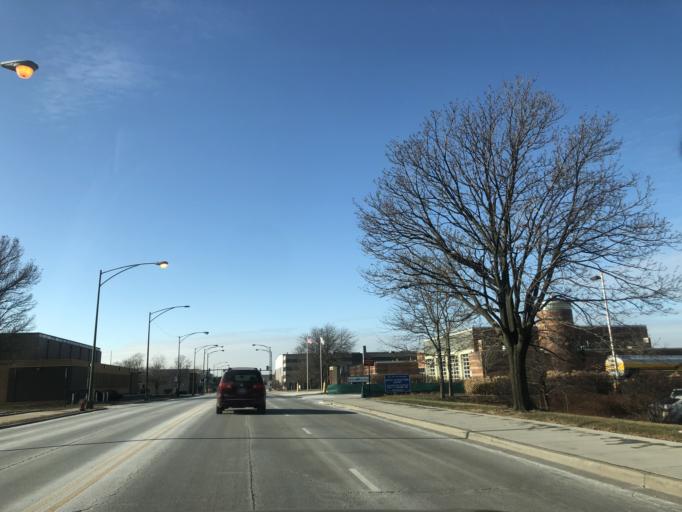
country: US
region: Illinois
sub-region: Cook County
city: Hometown
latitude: 41.7782
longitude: -87.7514
